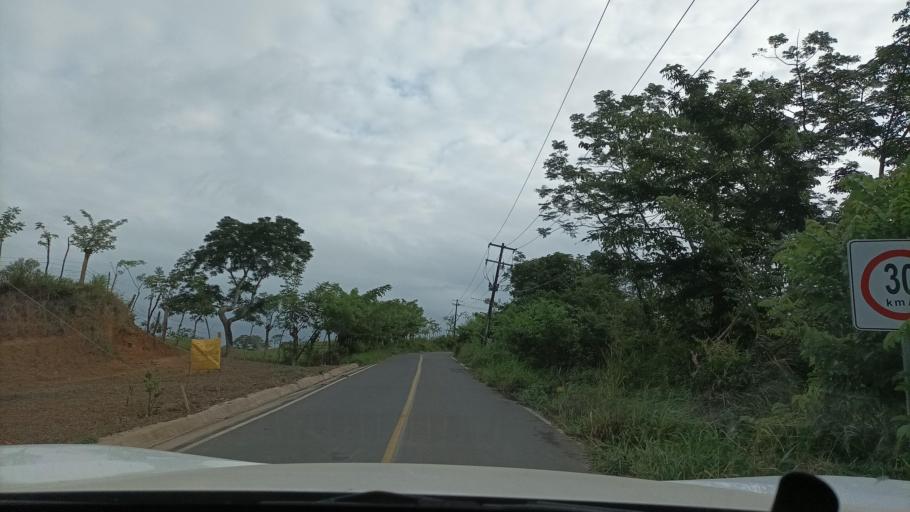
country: MX
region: Veracruz
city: Hidalgotitlan
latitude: 17.6866
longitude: -94.4676
